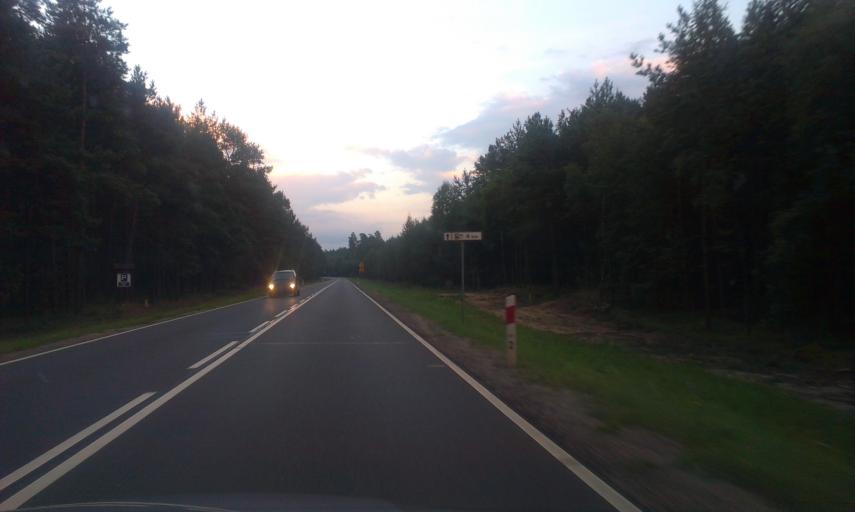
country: PL
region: West Pomeranian Voivodeship
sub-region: Powiat koszalinski
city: Sianow
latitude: 54.0701
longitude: 16.3988
